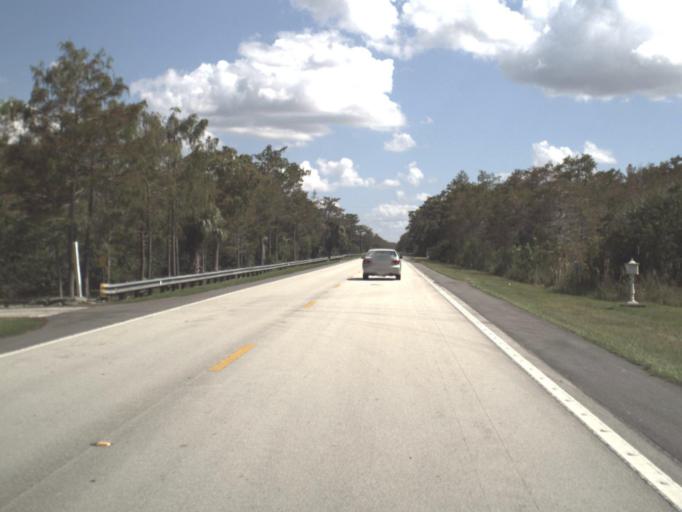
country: US
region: Florida
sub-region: Miami-Dade County
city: Kendall West
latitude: 25.8150
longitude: -80.8843
